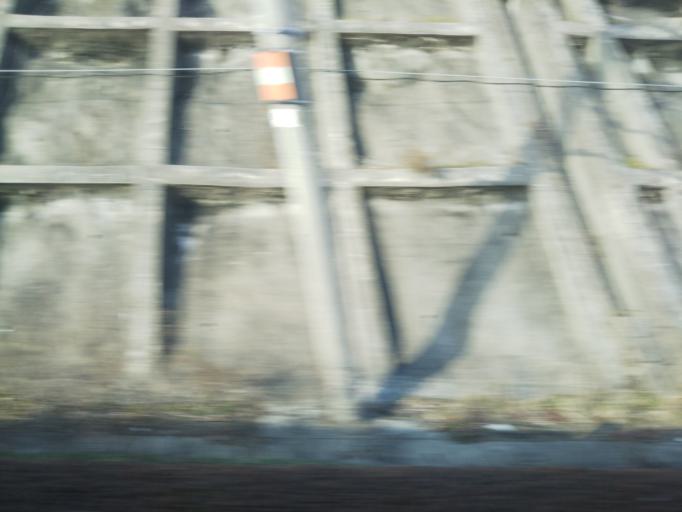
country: JP
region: Kagawa
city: Sakaidecho
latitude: 34.4472
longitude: 133.8082
